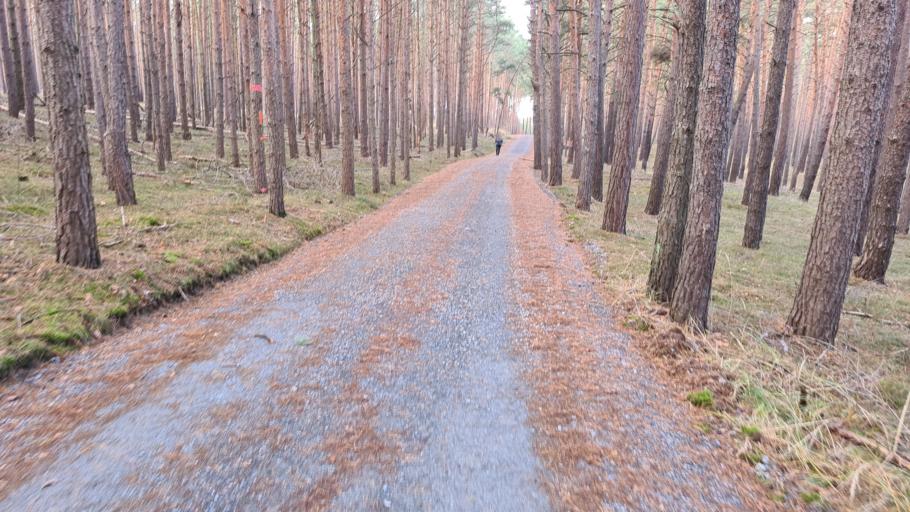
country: DE
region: Brandenburg
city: Groden
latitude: 51.3909
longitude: 13.5764
